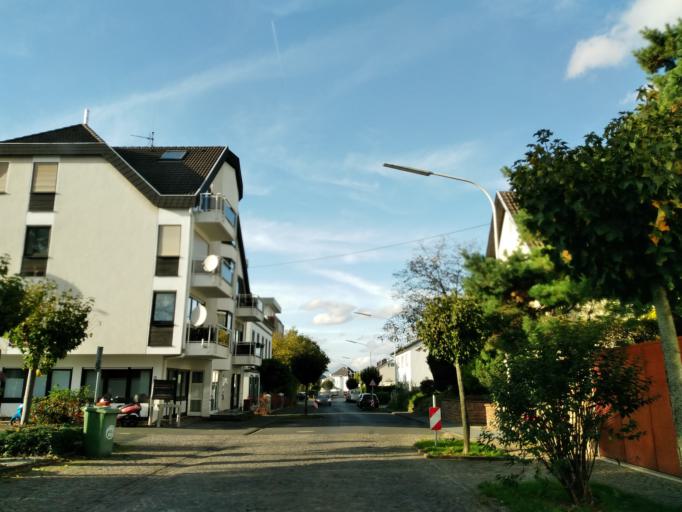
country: DE
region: Rheinland-Pfalz
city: Rheinbreitbach
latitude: 50.6199
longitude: 7.2307
